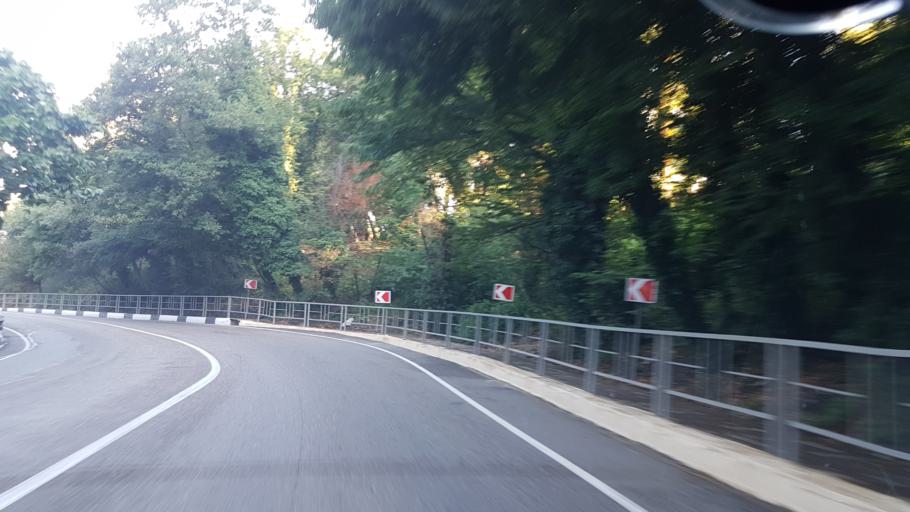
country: RU
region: Krasnodarskiy
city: Gornoye Loo
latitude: 43.6767
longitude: 39.6077
